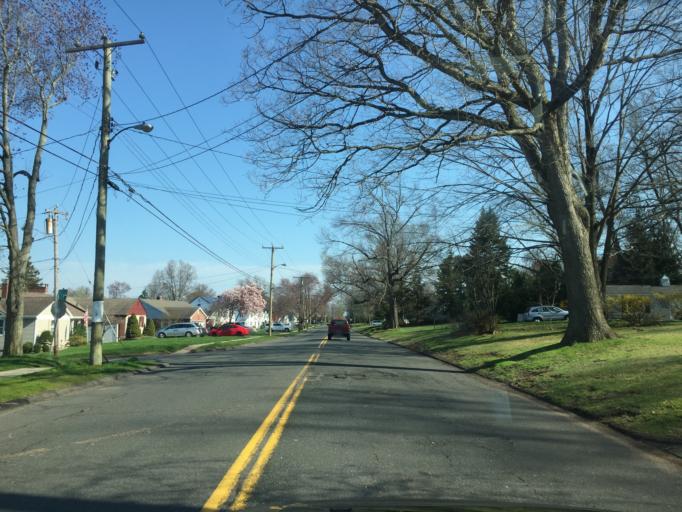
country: US
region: Connecticut
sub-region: Hartford County
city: Wethersfield
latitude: 41.6965
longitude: -72.6832
